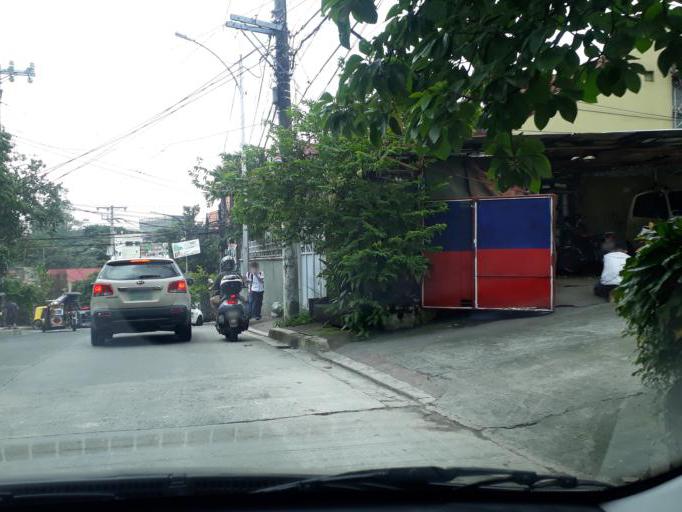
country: PH
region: Calabarzon
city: Del Monte
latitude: 14.6269
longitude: 121.0249
